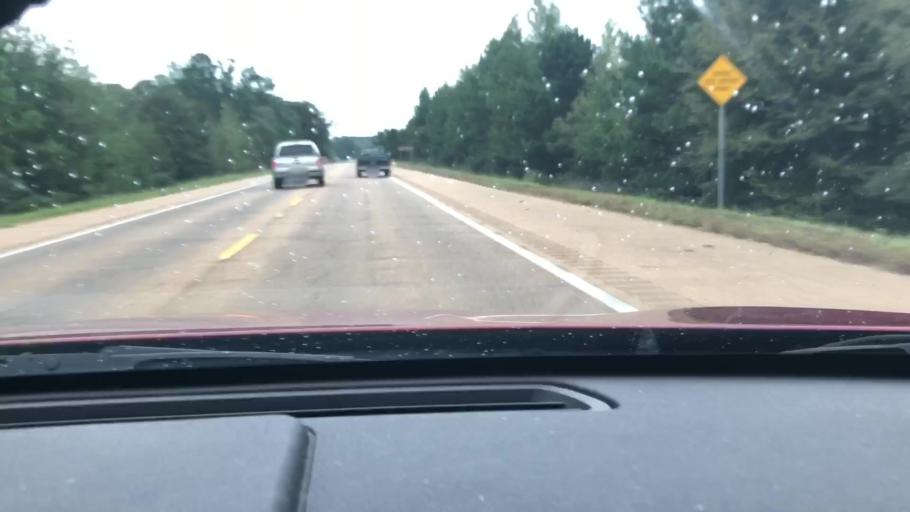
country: US
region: Arkansas
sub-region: Lafayette County
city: Stamps
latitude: 33.3667
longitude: -93.5253
